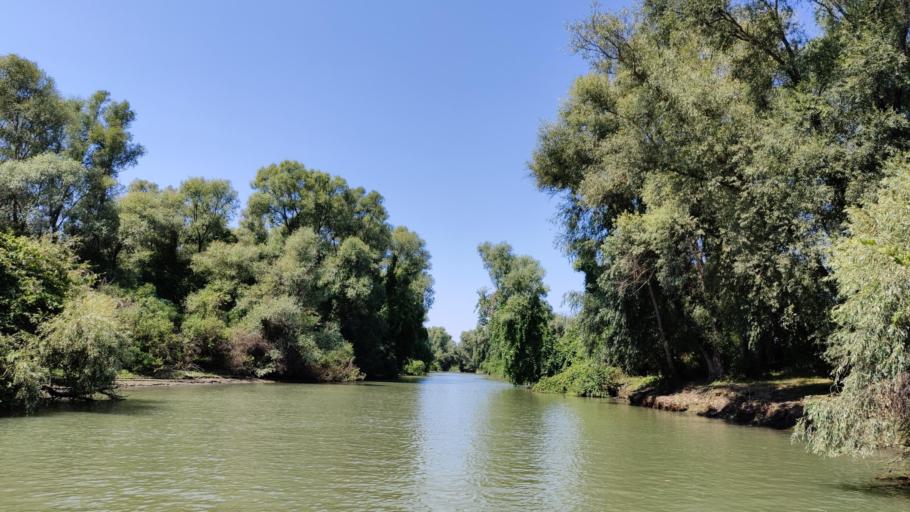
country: RO
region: Tulcea
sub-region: Comuna Pardina
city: Pardina
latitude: 45.2547
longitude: 28.9444
